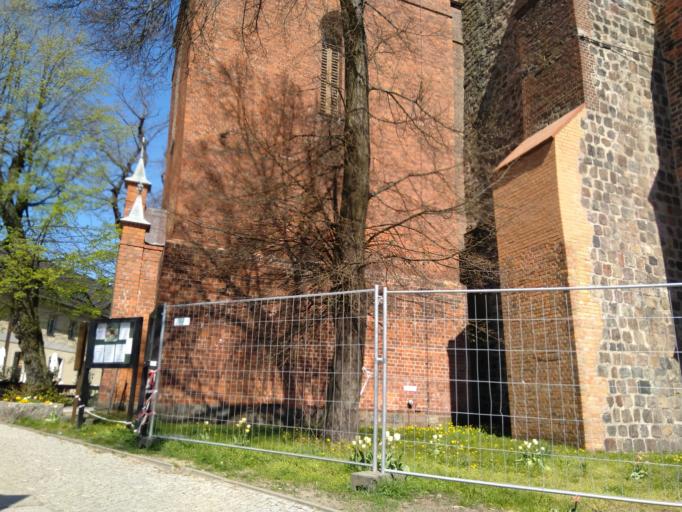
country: DE
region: Brandenburg
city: Bernau bei Berlin
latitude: 52.6796
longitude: 13.5867
